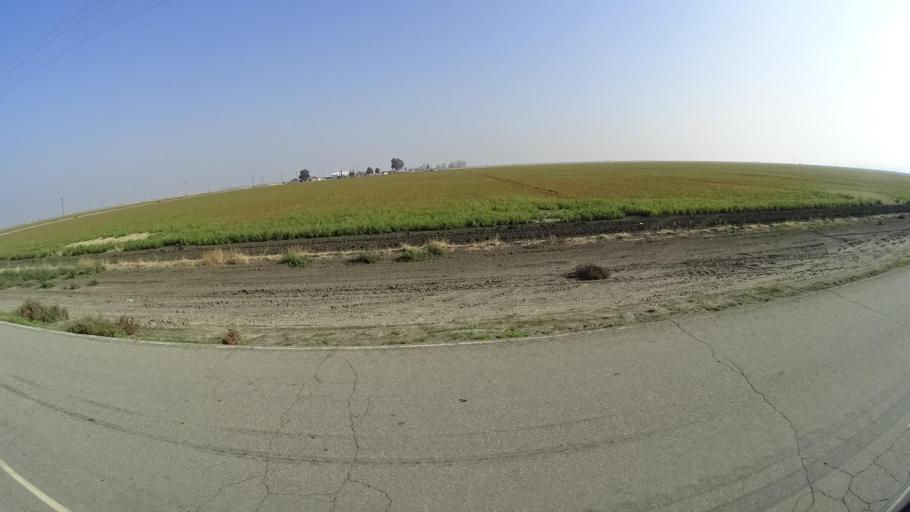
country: US
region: California
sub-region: Kern County
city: Buttonwillow
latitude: 35.3316
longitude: -119.3768
